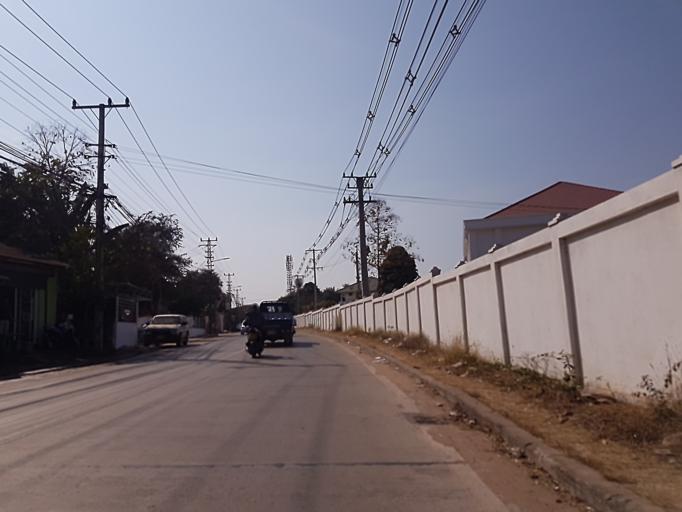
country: LA
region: Vientiane
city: Vientiane
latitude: 17.9452
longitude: 102.6333
